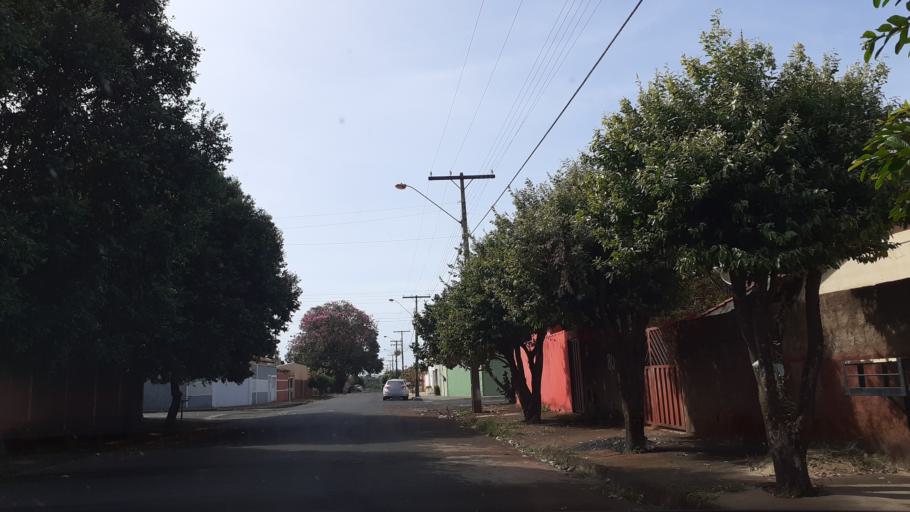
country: BR
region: Goias
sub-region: Itumbiara
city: Itumbiara
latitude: -18.4205
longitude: -49.2446
